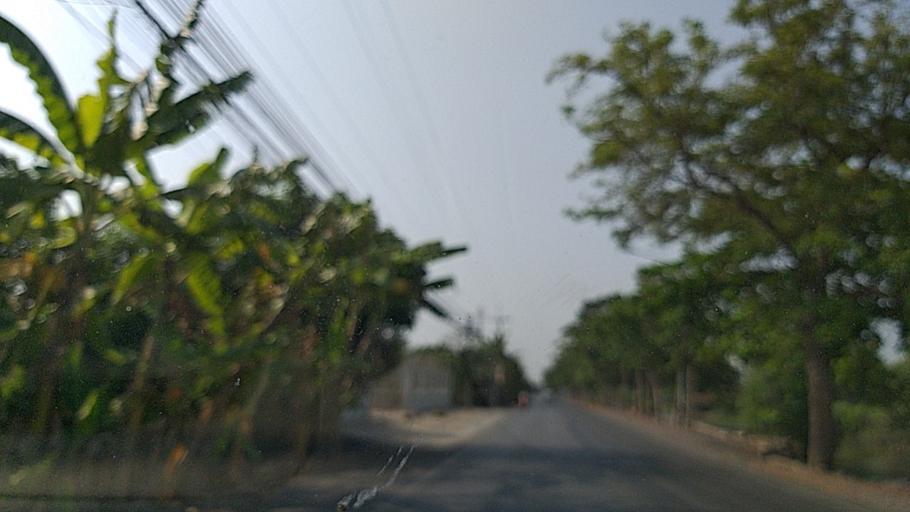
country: TH
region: Pathum Thani
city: Lam Luk Ka
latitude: 13.9469
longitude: 100.7059
